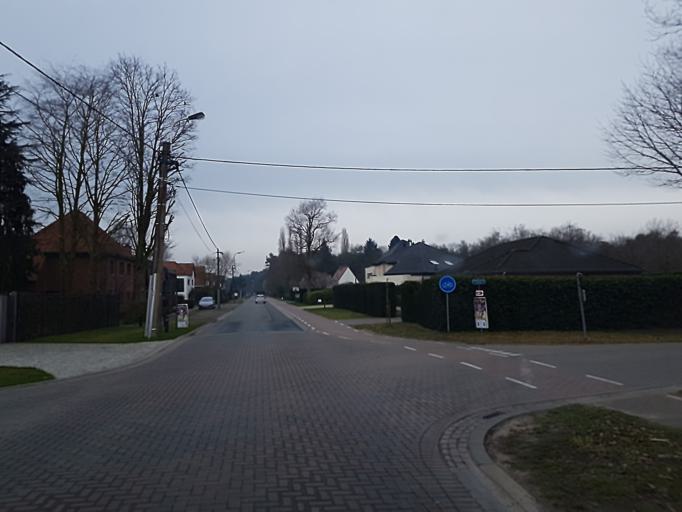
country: BE
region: Flanders
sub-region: Provincie Oost-Vlaanderen
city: Waarschoot
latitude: 51.1821
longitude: 3.6235
